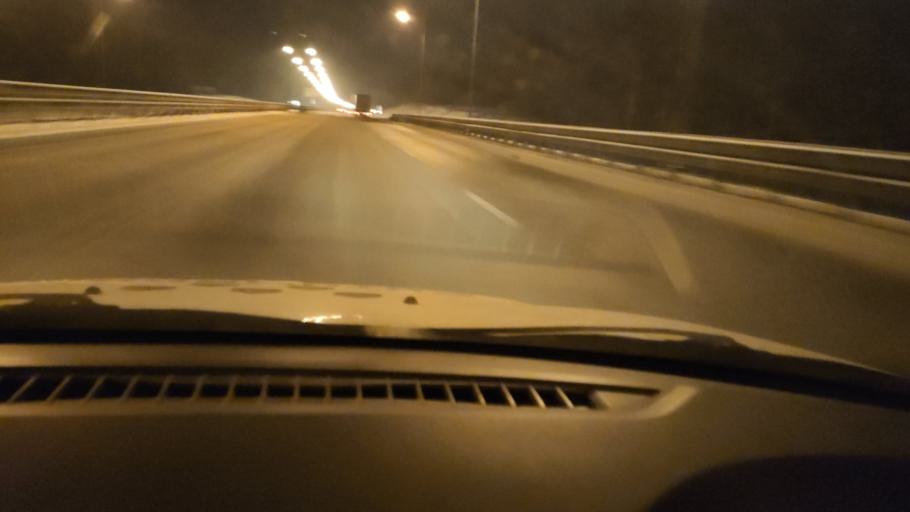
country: RU
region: Perm
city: Zvezdnyy
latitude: 57.7386
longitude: 56.3408
